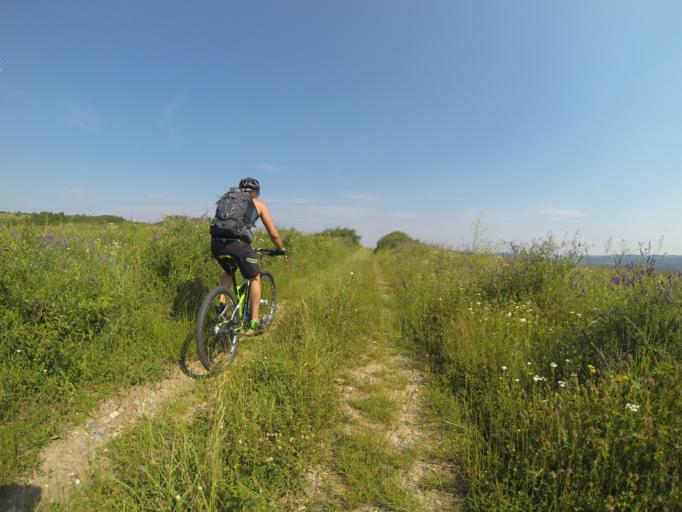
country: RO
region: Gorj
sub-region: Comuna Crusetu
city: Crusetu
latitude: 44.6086
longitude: 23.6697
